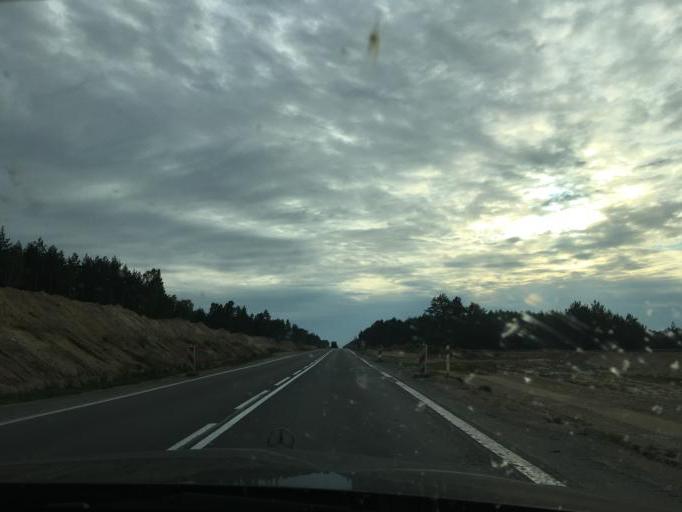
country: PL
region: Masovian Voivodeship
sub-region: Powiat ostrowski
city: Brok
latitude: 52.7500
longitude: 21.7789
